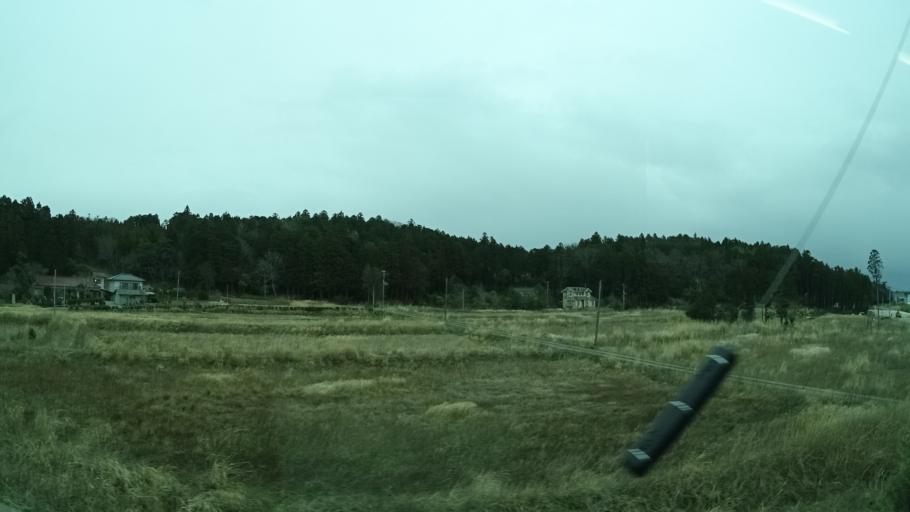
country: JP
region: Fukushima
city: Namie
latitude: 37.3415
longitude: 141.0200
